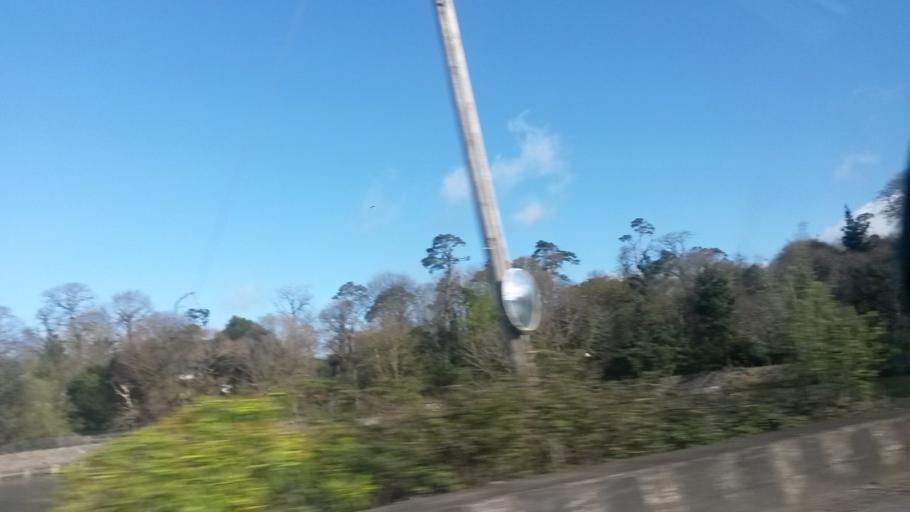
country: IE
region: Munster
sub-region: County Cork
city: Cobh
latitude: 51.8889
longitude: -8.3069
